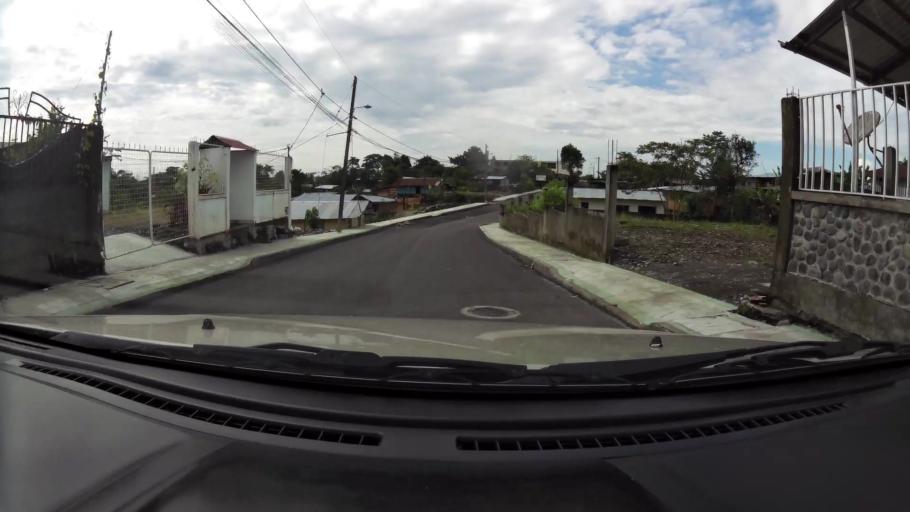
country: EC
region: Pastaza
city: Puyo
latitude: -1.4943
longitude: -77.9955
